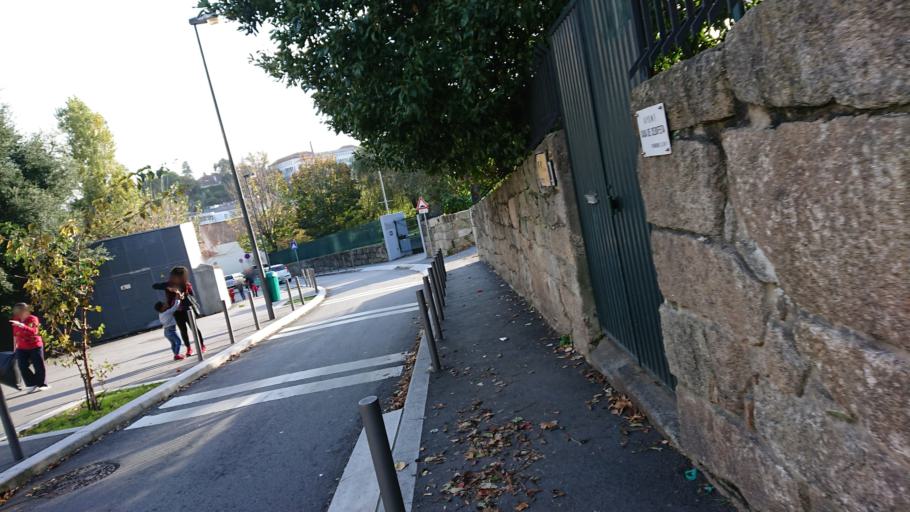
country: PT
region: Porto
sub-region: Porto
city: Porto
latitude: 41.1553
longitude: -8.6238
